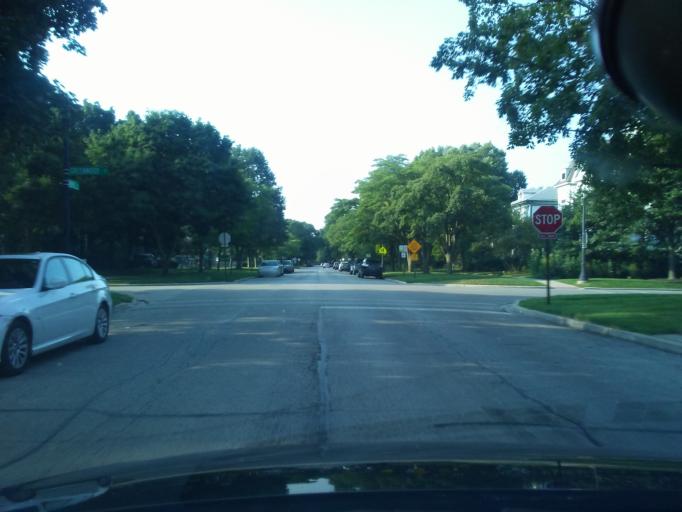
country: US
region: Illinois
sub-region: Cook County
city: Evanston
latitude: 42.0429
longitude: -87.6788
